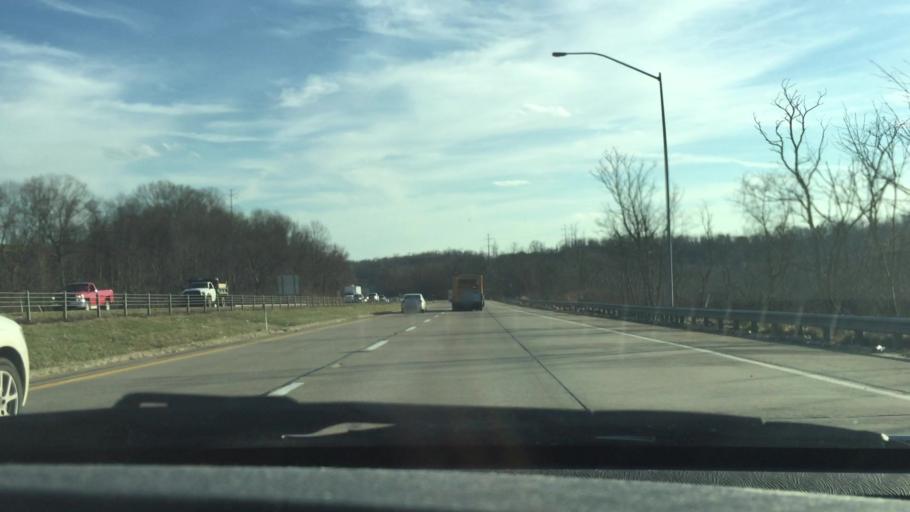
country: US
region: Pennsylvania
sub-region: Allegheny County
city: Carnegie
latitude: 40.4423
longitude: -80.1115
